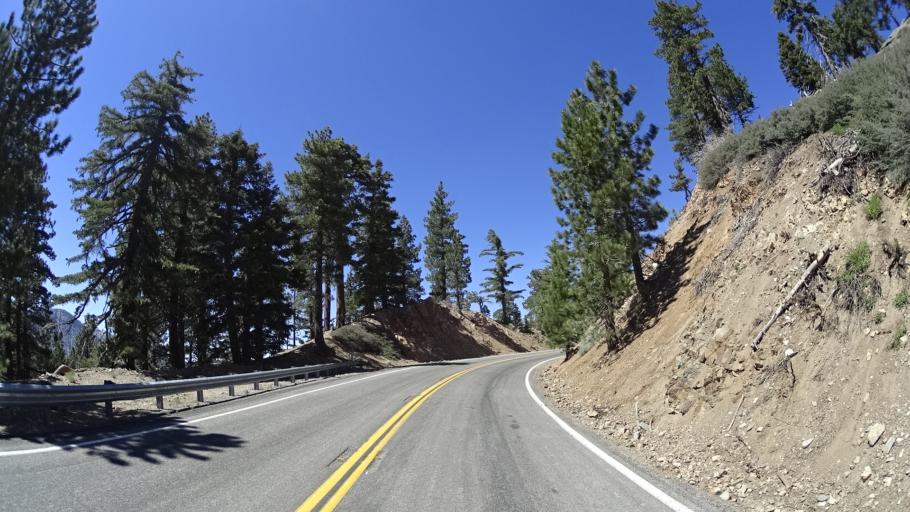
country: US
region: California
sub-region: San Bernardino County
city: Wrightwood
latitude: 34.3492
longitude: -117.8199
